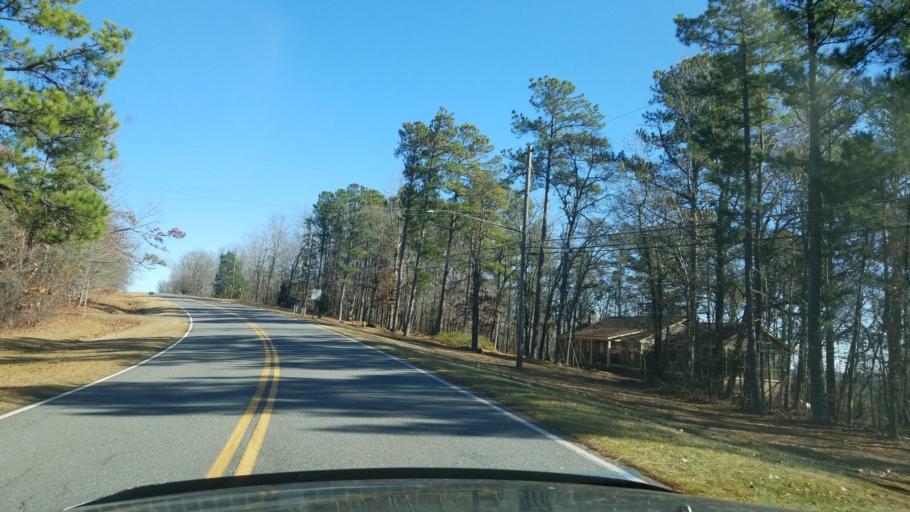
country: US
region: Georgia
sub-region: Meriwether County
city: Manchester
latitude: 32.8432
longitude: -84.6424
